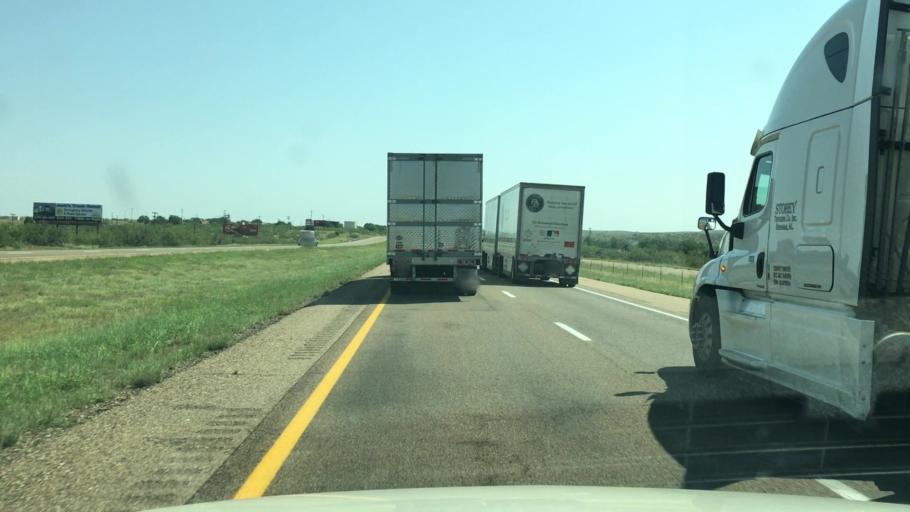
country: US
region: New Mexico
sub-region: Quay County
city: Tucumcari
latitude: 35.1450
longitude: -103.8072
